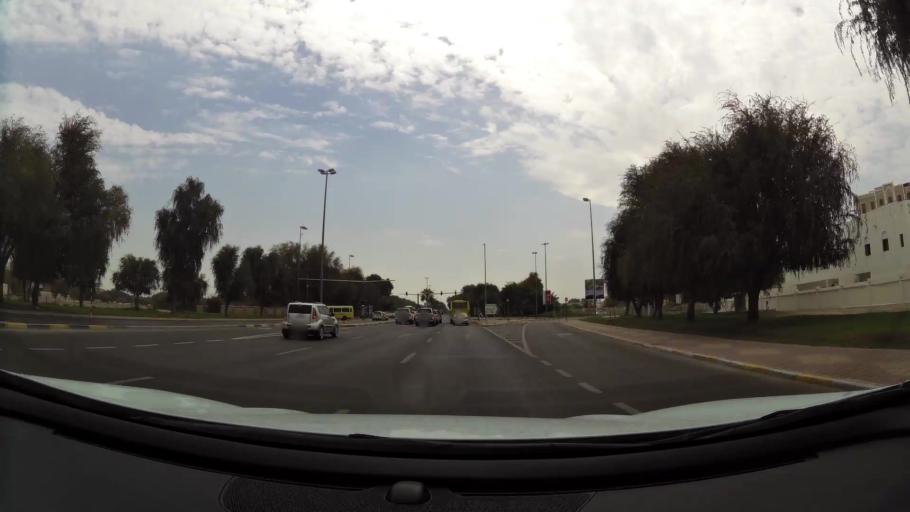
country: OM
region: Al Buraimi
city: Al Buraymi
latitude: 24.2255
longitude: 55.7845
